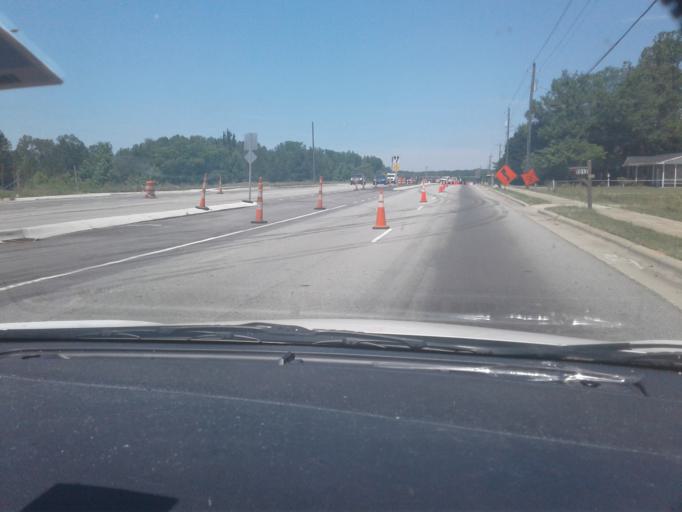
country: US
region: North Carolina
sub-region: Wake County
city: Fuquay-Varina
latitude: 35.6134
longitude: -78.8084
